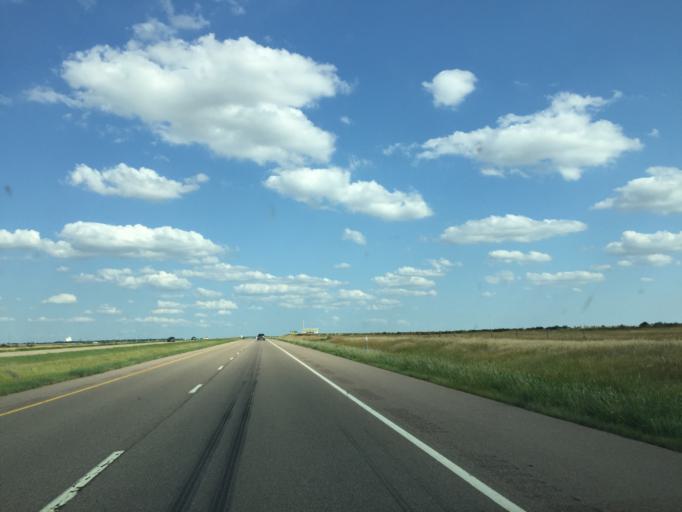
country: US
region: Kansas
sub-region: Gove County
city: Gove
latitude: 39.0837
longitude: -100.2968
